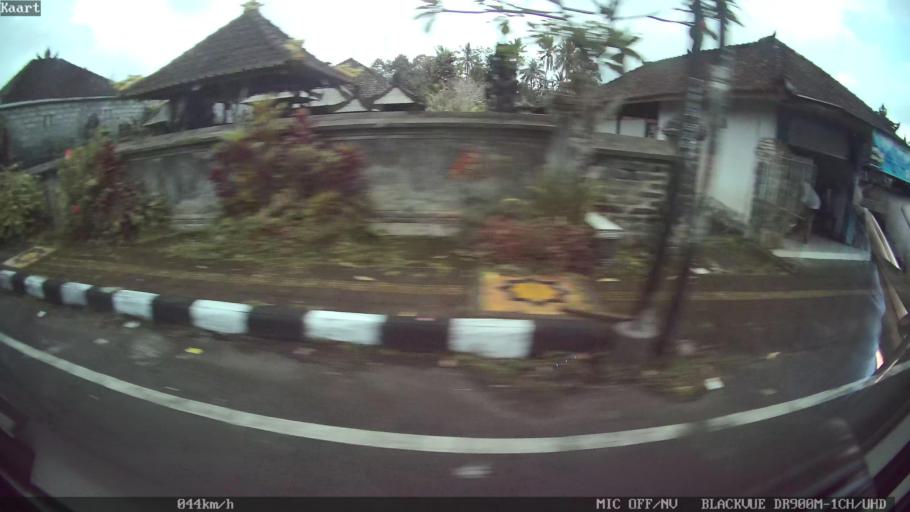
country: ID
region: Bali
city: Penebel
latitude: -8.4242
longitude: 115.1446
